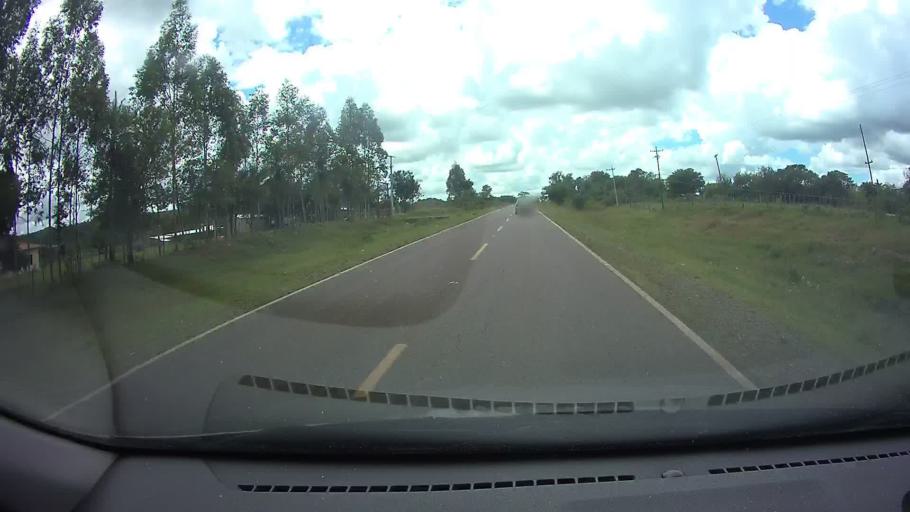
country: PY
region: Paraguari
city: La Colmena
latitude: -25.8962
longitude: -56.9542
